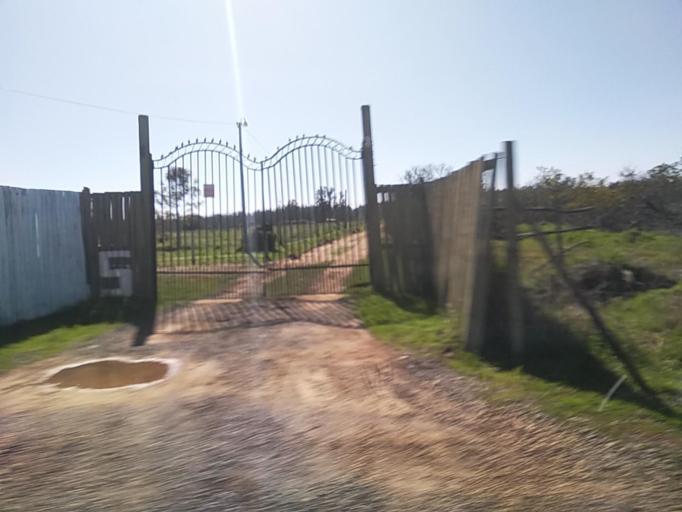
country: CL
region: Valparaiso
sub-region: San Antonio Province
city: El Tabo
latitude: -33.4097
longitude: -71.5968
